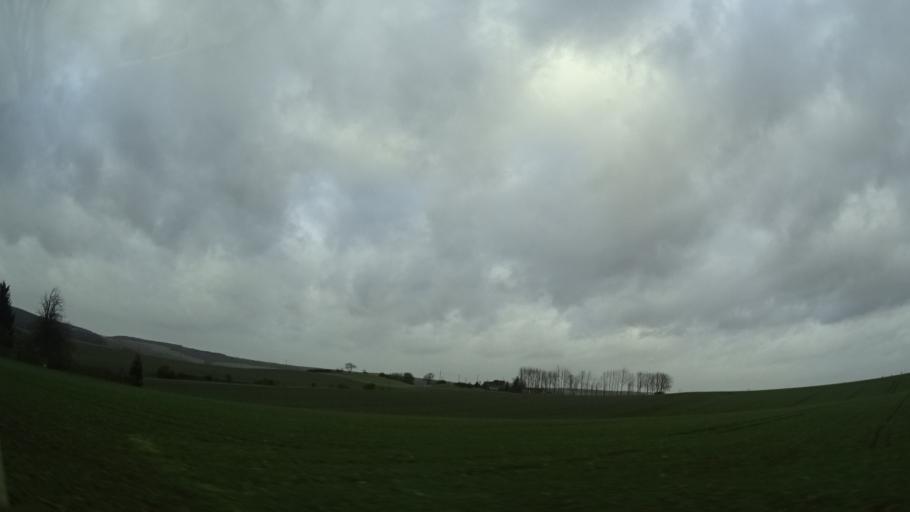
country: DE
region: Thuringia
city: Dreitzsch
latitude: 50.7261
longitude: 11.7901
